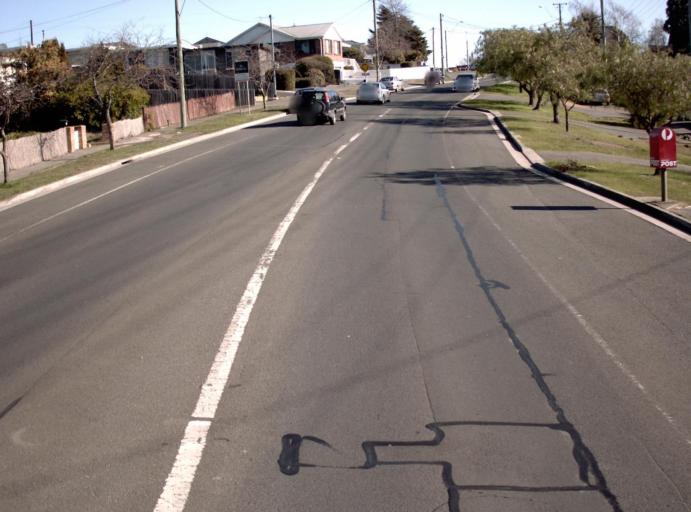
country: AU
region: Tasmania
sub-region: Launceston
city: Summerhill
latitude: -41.4729
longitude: 147.1303
